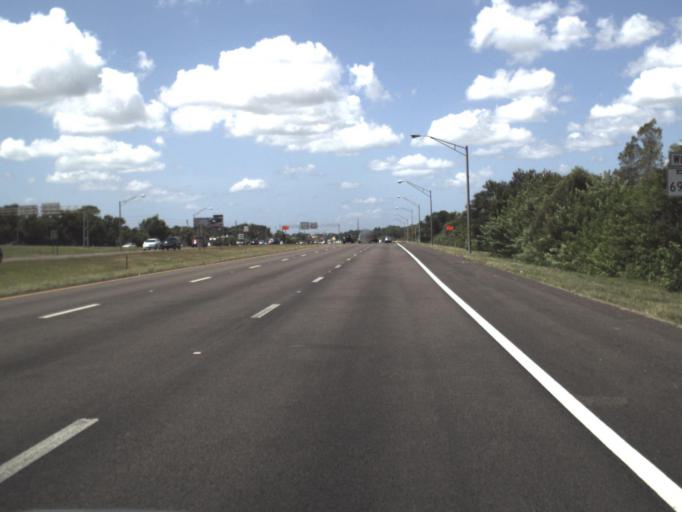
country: US
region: Florida
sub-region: Pinellas County
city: Lealman
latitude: 27.8520
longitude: -82.6653
